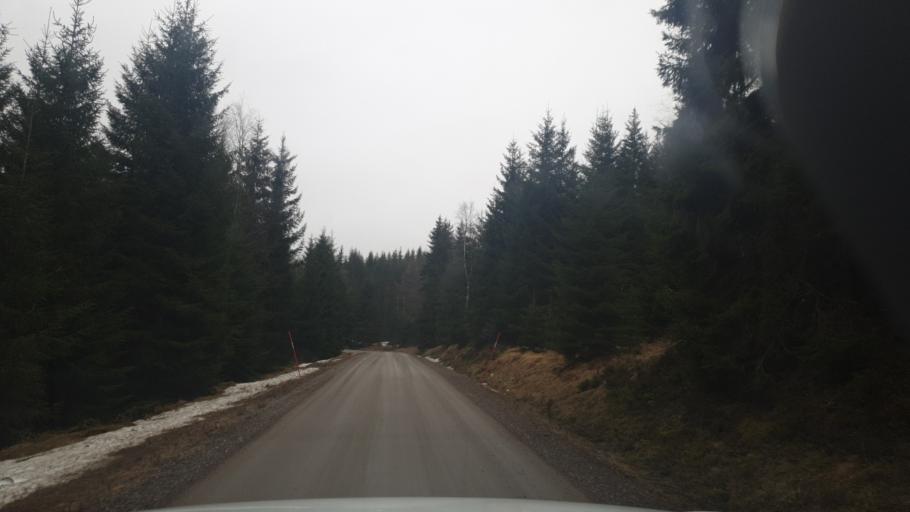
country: NO
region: Ostfold
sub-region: Romskog
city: Romskog
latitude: 59.7136
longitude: 11.9997
